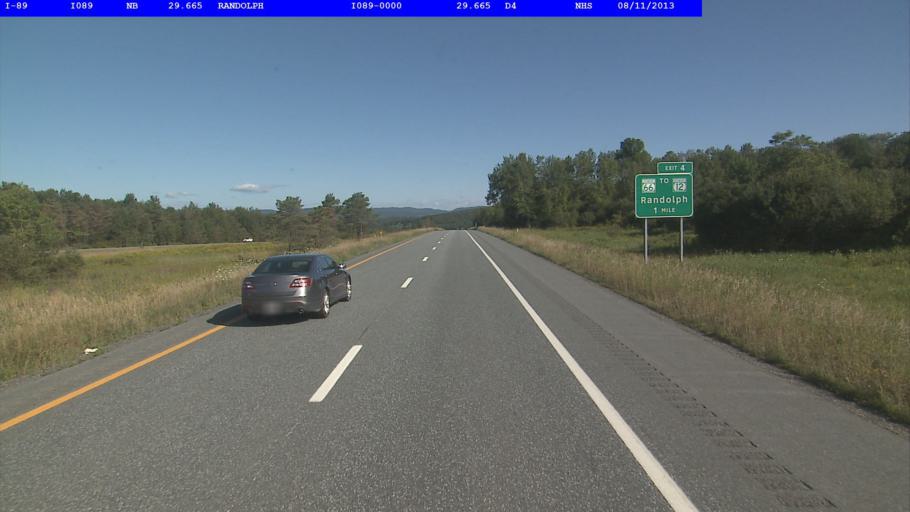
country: US
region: Vermont
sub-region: Orange County
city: Randolph
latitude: 43.9272
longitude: -72.6168
